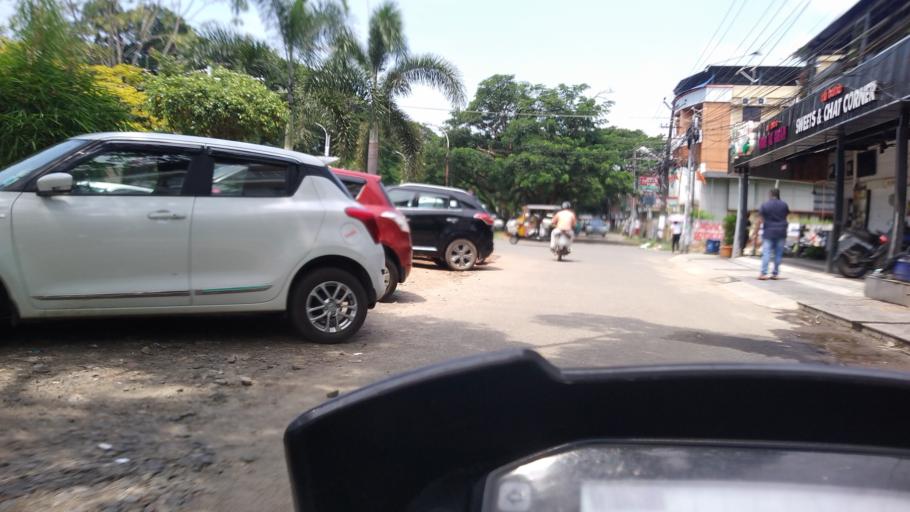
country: IN
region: Kerala
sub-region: Ernakulam
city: Cochin
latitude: 9.9594
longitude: 76.2962
